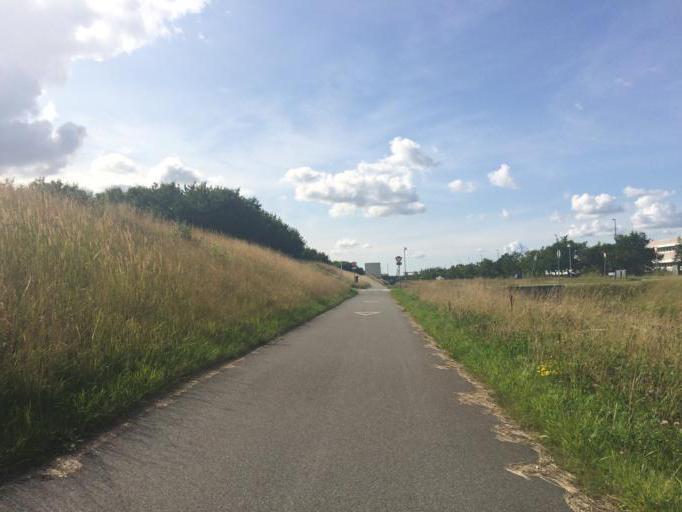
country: DK
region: Capital Region
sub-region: Hvidovre Kommune
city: Hvidovre
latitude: 55.6053
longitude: 12.4745
